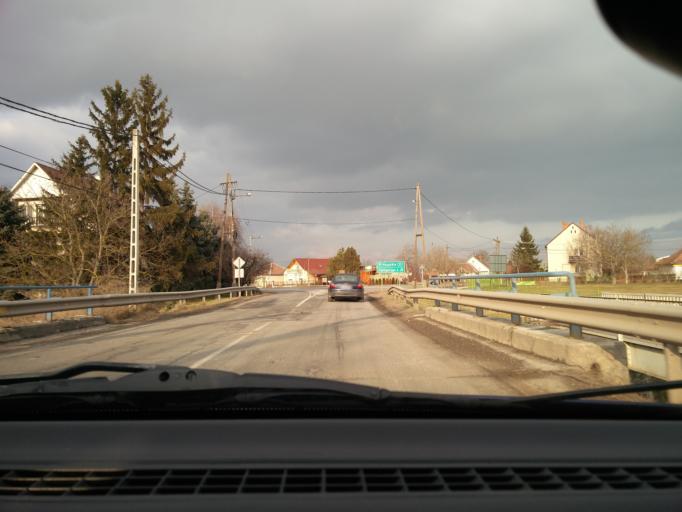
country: HU
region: Pest
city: Tapioszele
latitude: 47.3237
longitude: 19.8766
